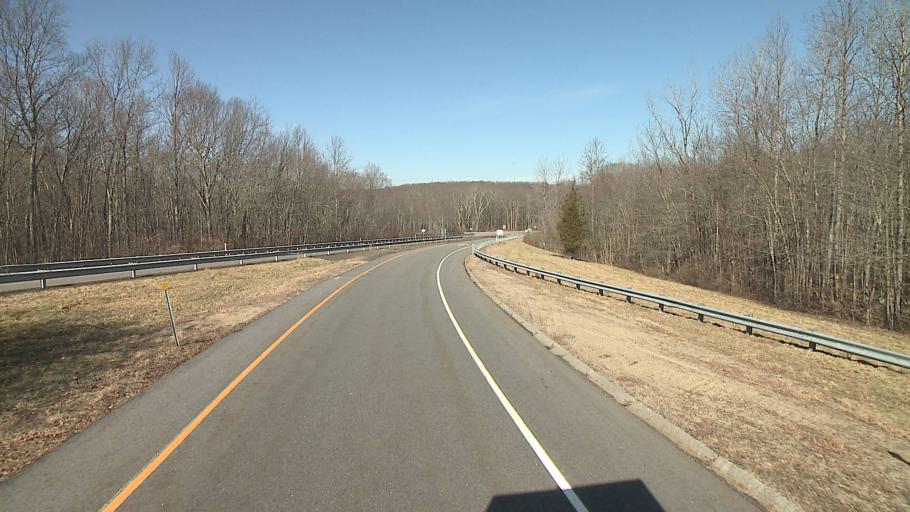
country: US
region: Connecticut
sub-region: New London County
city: Colchester
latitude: 41.5734
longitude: -72.2953
